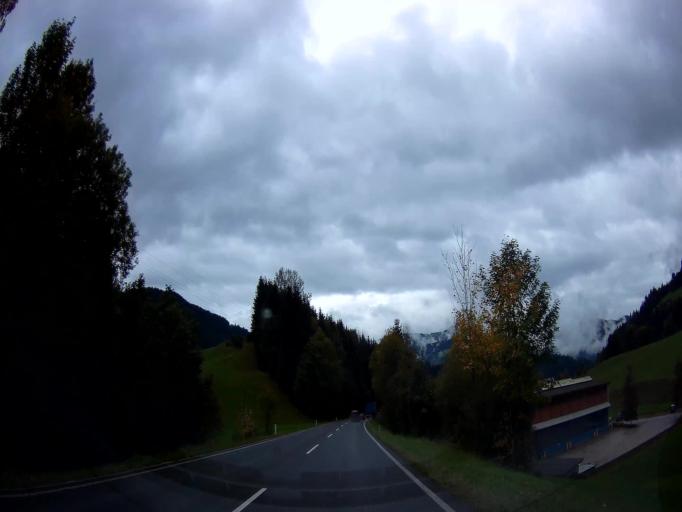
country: AT
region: Tyrol
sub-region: Politischer Bezirk Kufstein
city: Soll
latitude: 47.4891
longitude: 12.1653
